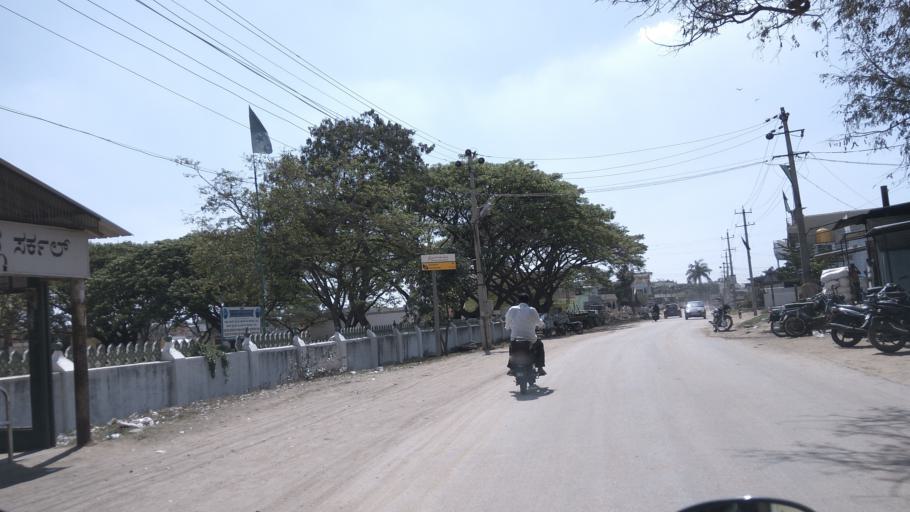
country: IN
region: Karnataka
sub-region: Kolar
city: Mulbagal
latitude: 13.1623
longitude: 78.3845
